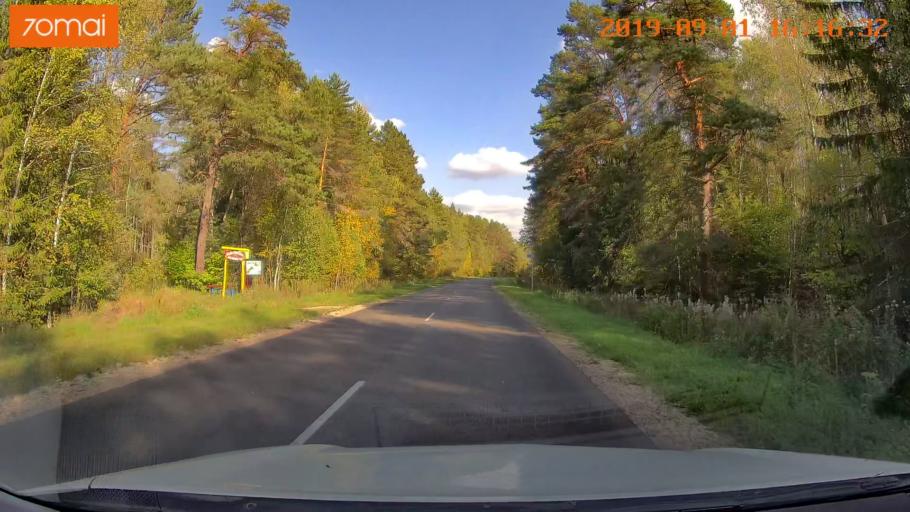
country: RU
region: Kaluga
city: Maloyaroslavets
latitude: 54.9134
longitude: 36.4916
